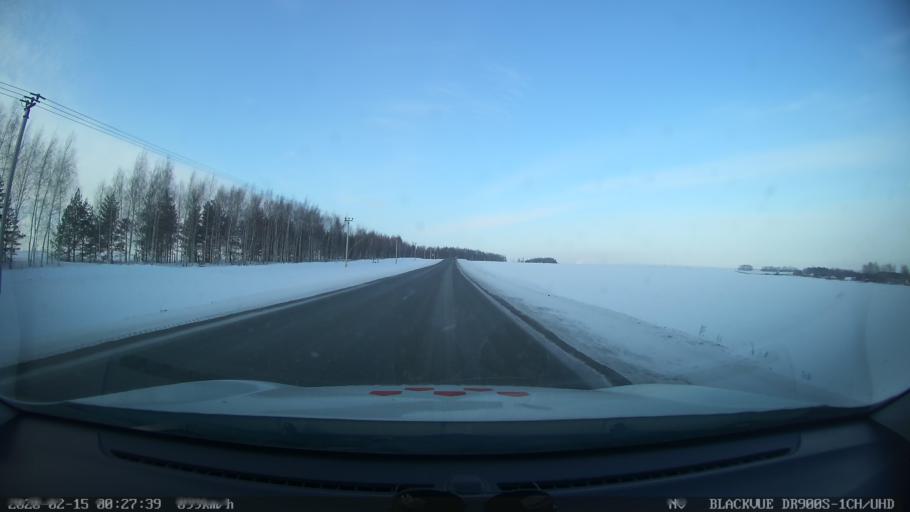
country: RU
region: Tatarstan
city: Verkhniy Uslon
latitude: 55.6311
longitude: 48.8726
